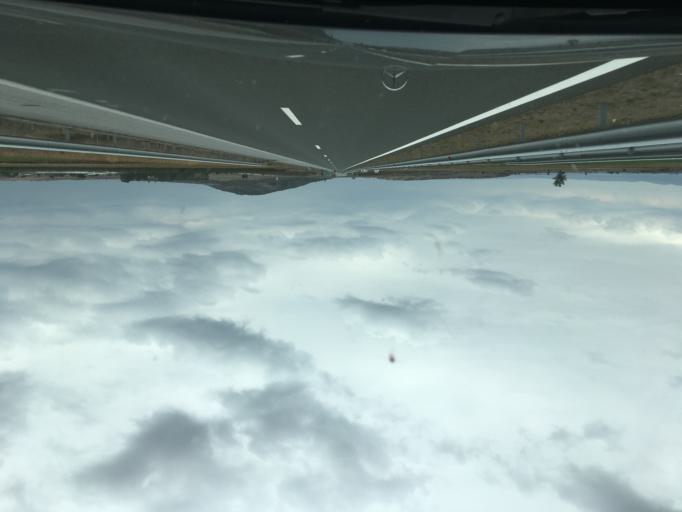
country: BG
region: Yambol
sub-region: Obshtina Yambol
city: Yambol
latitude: 42.5419
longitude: 26.4345
